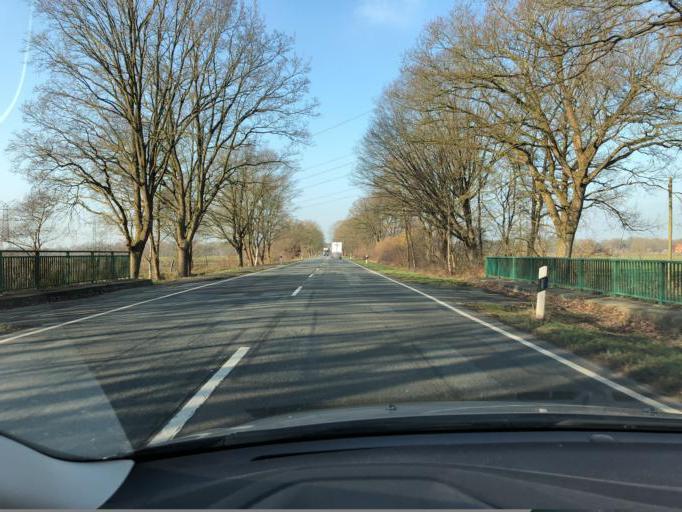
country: DE
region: Lower Saxony
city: Westerstede
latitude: 53.2938
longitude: 7.8498
